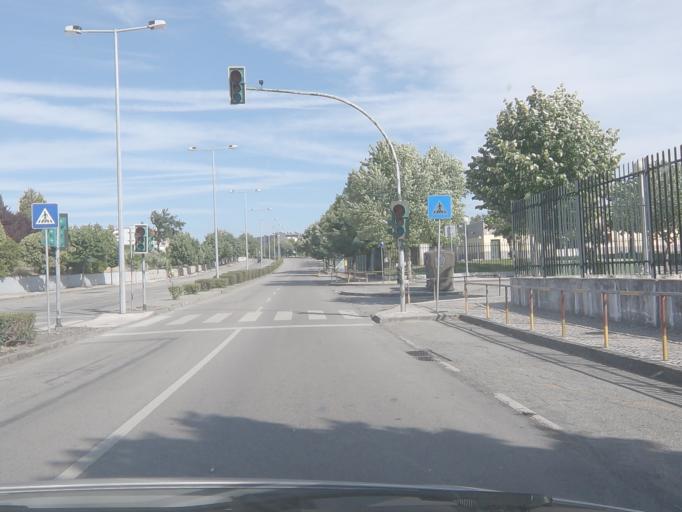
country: PT
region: Viseu
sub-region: Viseu
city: Viseu
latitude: 40.6429
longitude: -7.9210
